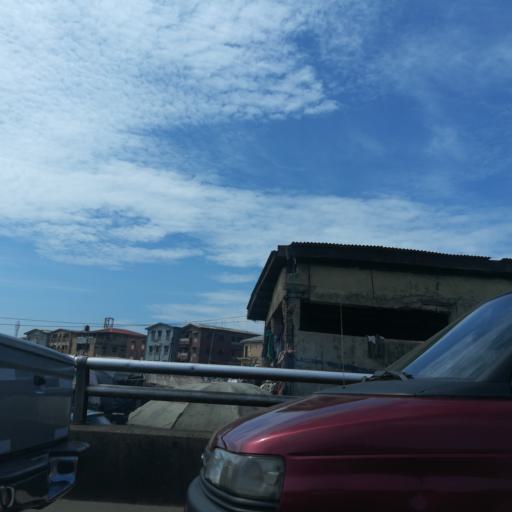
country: NG
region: Lagos
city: Lagos
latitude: 6.4658
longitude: 3.3912
